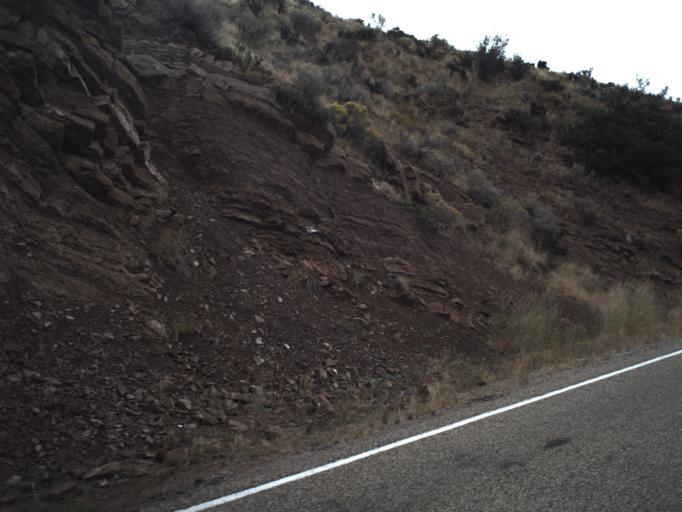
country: US
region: Utah
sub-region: Morgan County
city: Morgan
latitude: 40.9259
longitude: -111.5926
